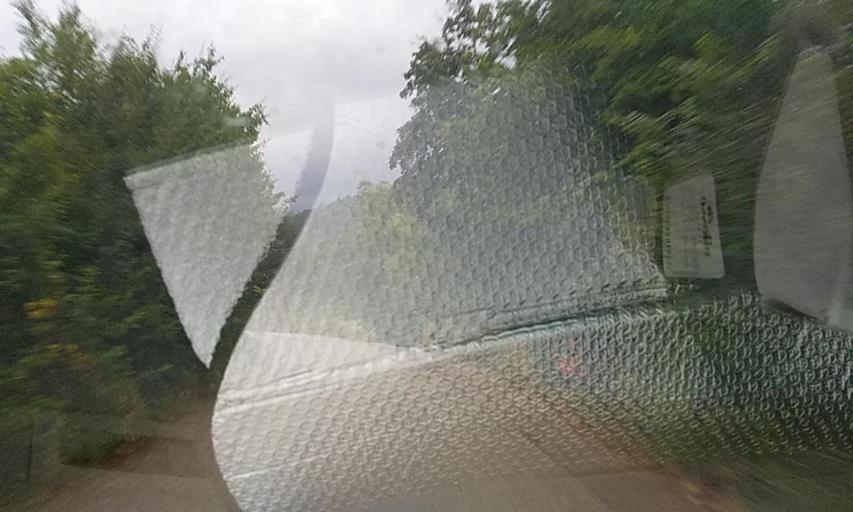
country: RS
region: Central Serbia
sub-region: Pirotski Okrug
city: Bela Palanka
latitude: 43.2283
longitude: 22.1976
